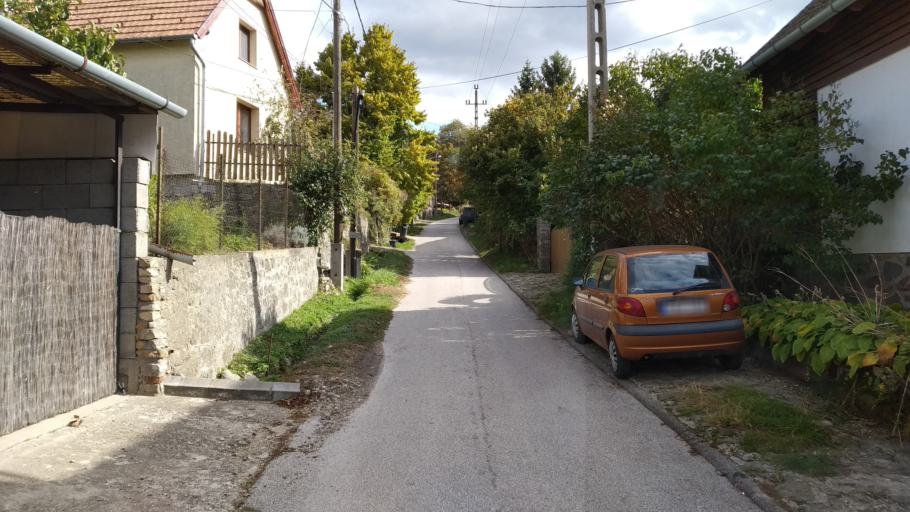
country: HU
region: Pest
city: Visegrad
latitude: 47.7224
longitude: 18.9913
